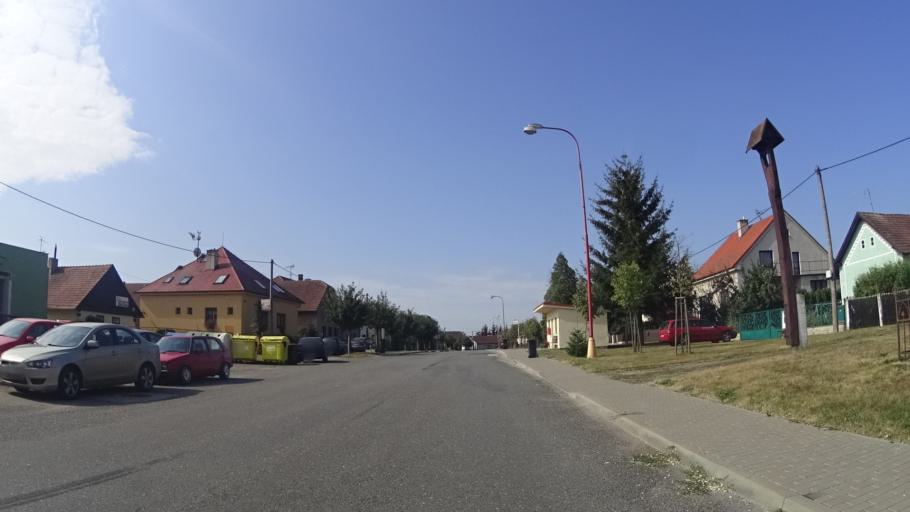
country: CZ
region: Kralovehradecky
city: Stare Nechanice
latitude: 50.2785
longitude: 15.5555
